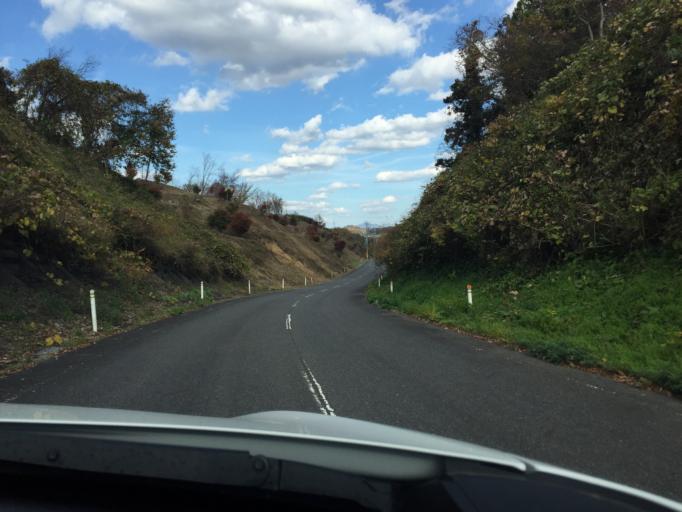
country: JP
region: Fukushima
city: Miharu
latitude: 37.4069
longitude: 140.4737
